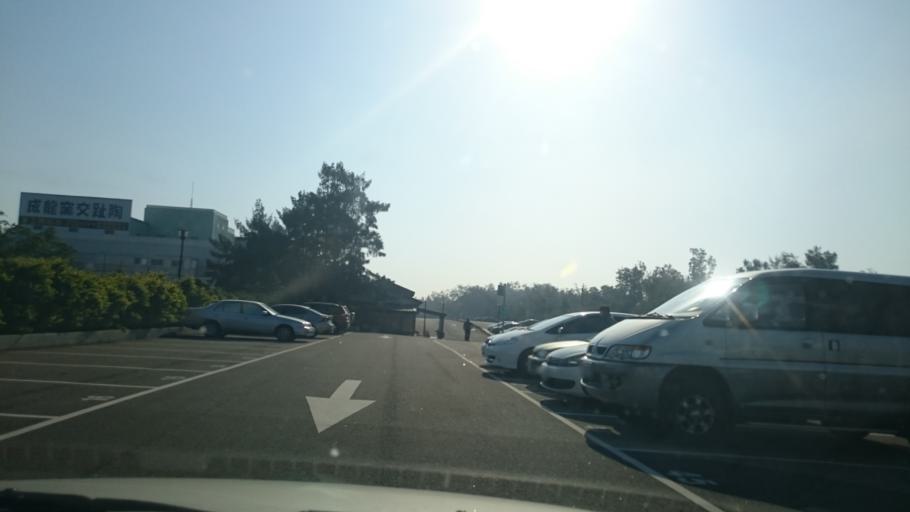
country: TW
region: Taiwan
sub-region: Miaoli
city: Miaoli
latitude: 24.6997
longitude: 120.8600
